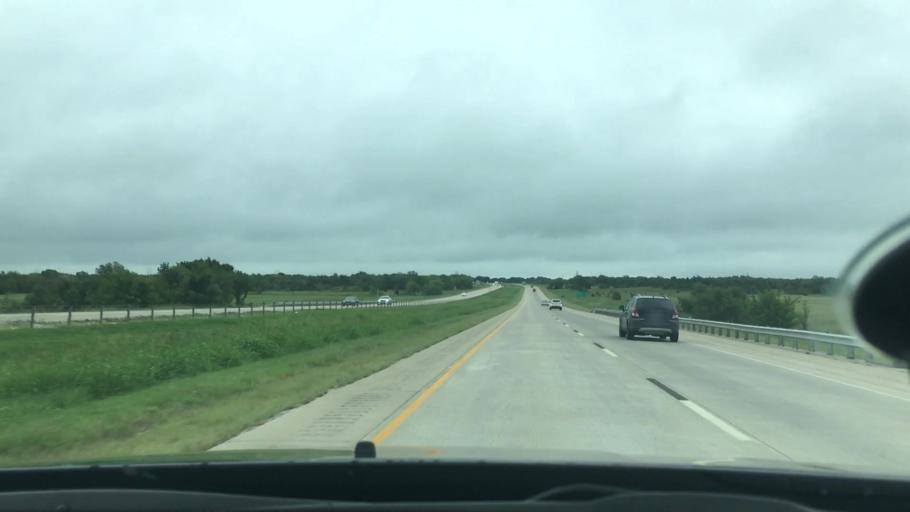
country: US
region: Oklahoma
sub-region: Okmulgee County
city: Wilson
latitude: 35.4301
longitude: -96.1105
